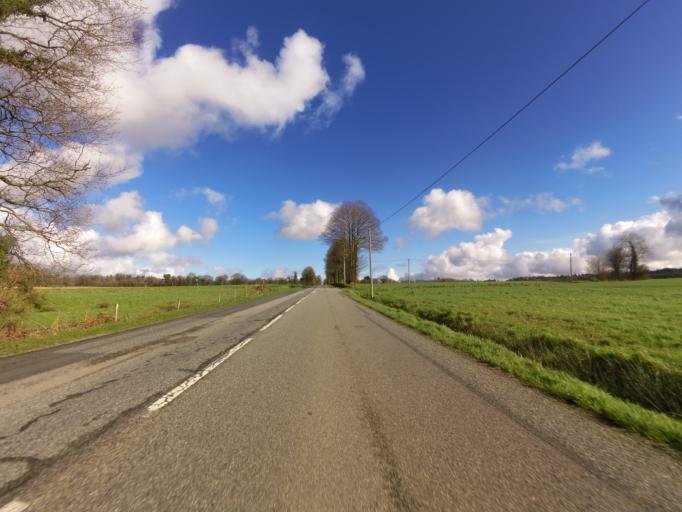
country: FR
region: Brittany
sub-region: Departement du Morbihan
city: Cleguerec
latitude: 48.0923
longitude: -3.0914
